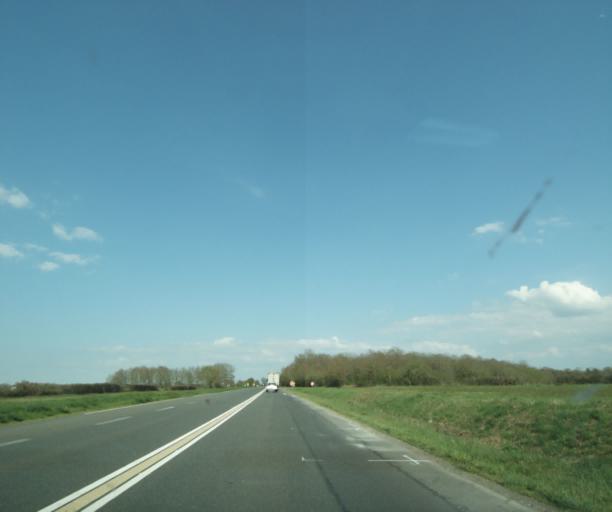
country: FR
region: Auvergne
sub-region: Departement de l'Allier
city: Lusigny
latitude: 46.5255
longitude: 3.4950
